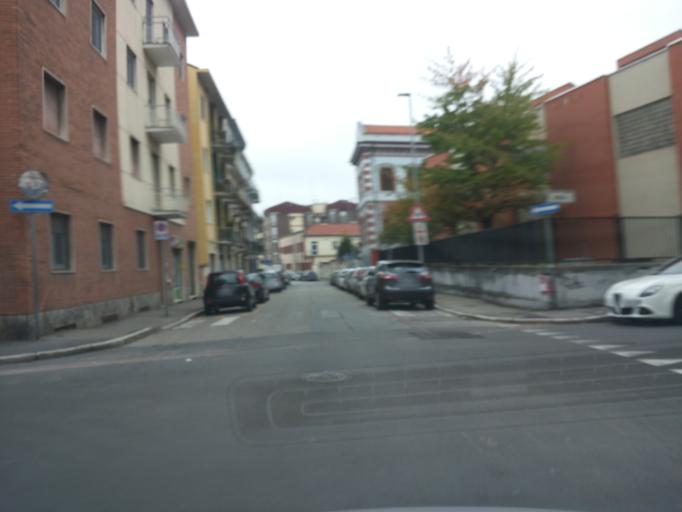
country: IT
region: Piedmont
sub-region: Provincia di Novara
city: Novara
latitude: 45.4436
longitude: 8.6100
